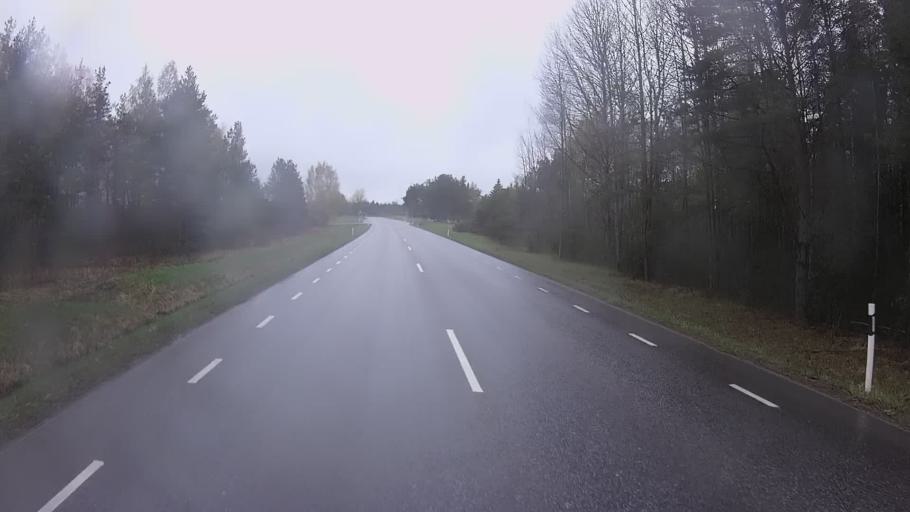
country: EE
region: Hiiumaa
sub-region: Kaerdla linn
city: Kardla
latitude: 58.9848
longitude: 22.5124
